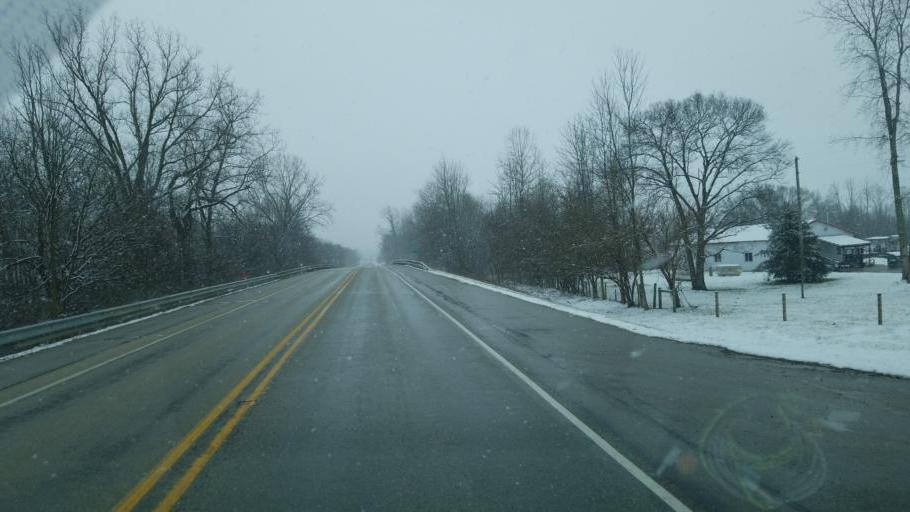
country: US
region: Indiana
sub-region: Wayne County
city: Centerville
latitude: 39.9068
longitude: -84.9521
